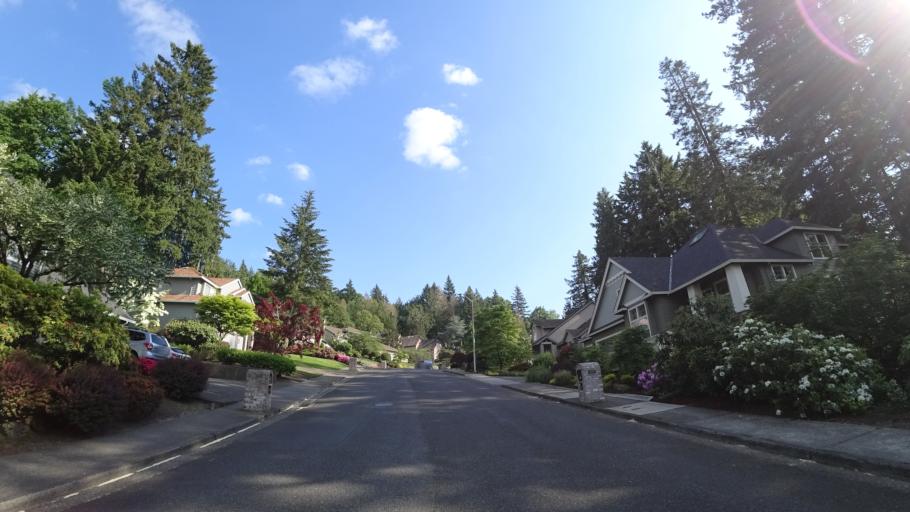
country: US
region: Oregon
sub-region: Washington County
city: Garden Home-Whitford
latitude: 45.4601
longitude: -122.7409
